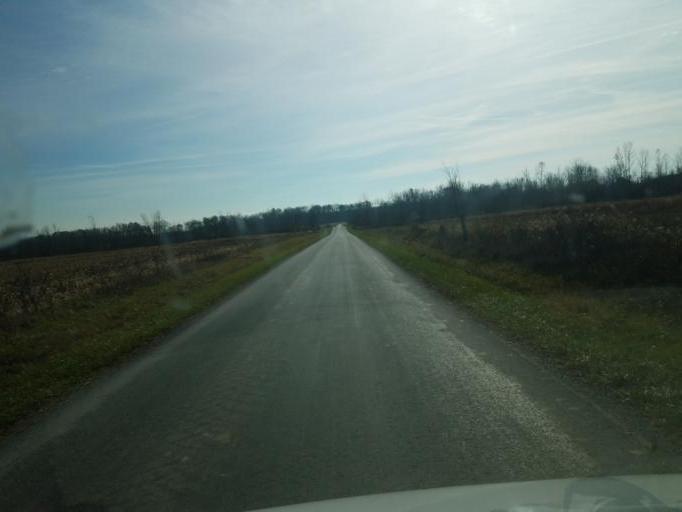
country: US
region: Ohio
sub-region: Hardin County
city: Kenton
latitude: 40.6152
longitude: -83.4385
